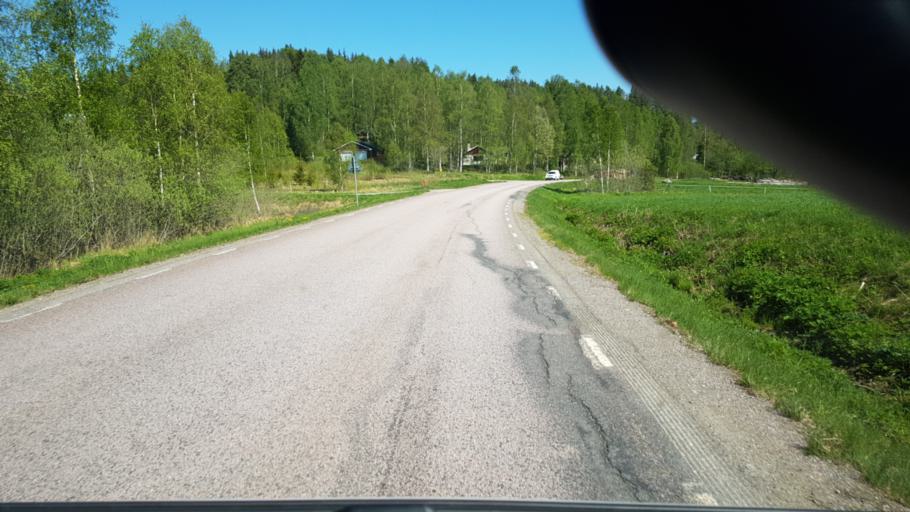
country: SE
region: Vaermland
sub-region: Eda Kommun
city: Amotfors
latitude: 59.8729
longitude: 12.5041
